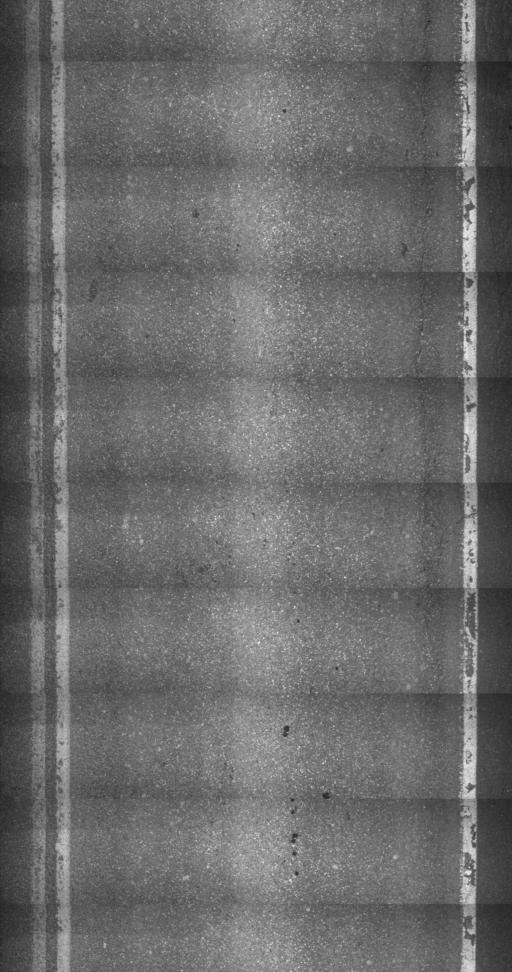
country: US
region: Vermont
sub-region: Chittenden County
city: Hinesburg
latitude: 44.3864
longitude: -73.1277
